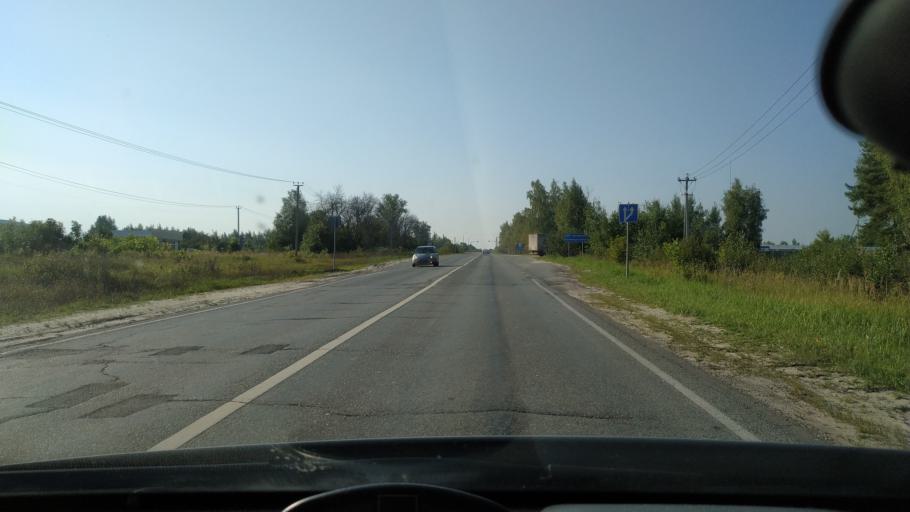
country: RU
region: Moskovskaya
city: Tugolesskiy Bor
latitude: 55.5555
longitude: 39.7028
